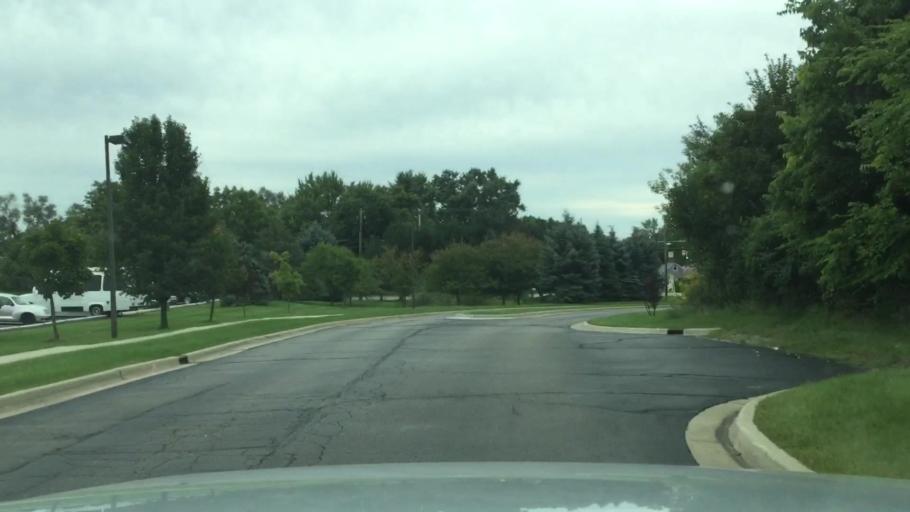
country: US
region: Michigan
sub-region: Genesee County
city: Swartz Creek
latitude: 42.9583
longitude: -83.8404
